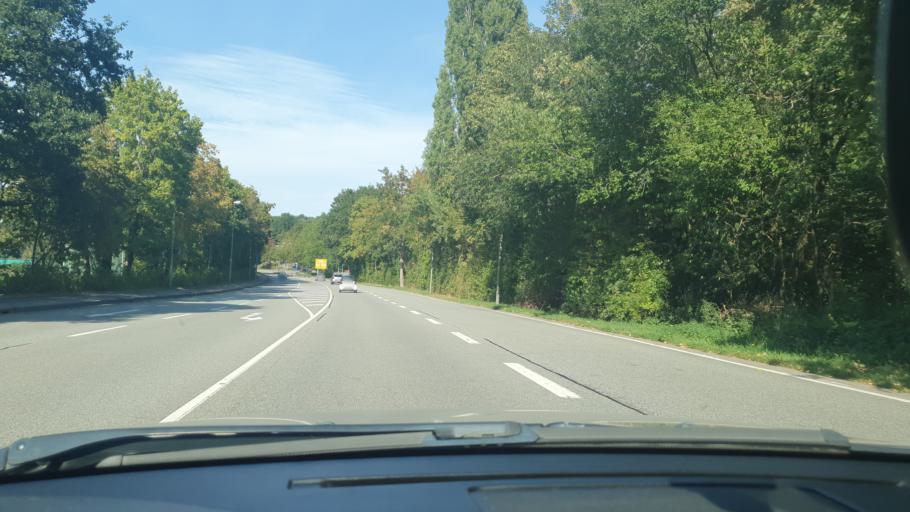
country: DE
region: Rheinland-Pfalz
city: Zweibrucken
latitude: 49.2545
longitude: 7.3799
